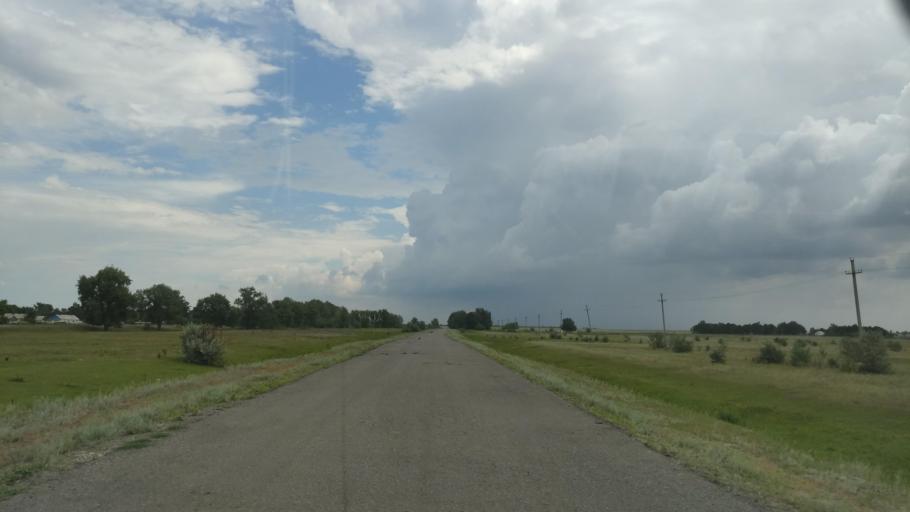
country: KZ
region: Pavlodar
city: Pavlodar
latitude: 52.6361
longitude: 77.3219
